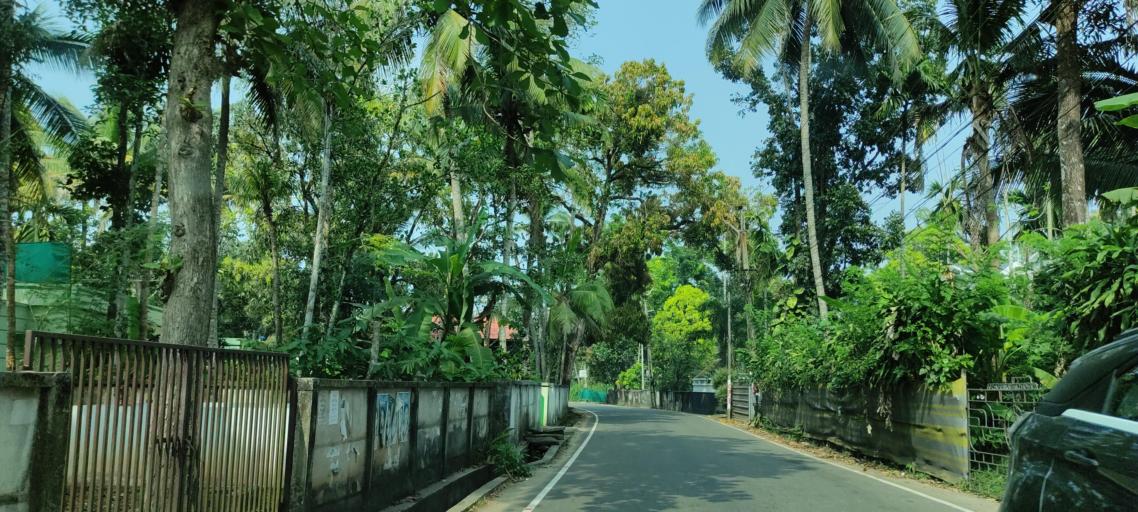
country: IN
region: Kerala
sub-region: Kottayam
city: Vaikam
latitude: 9.7507
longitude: 76.4022
